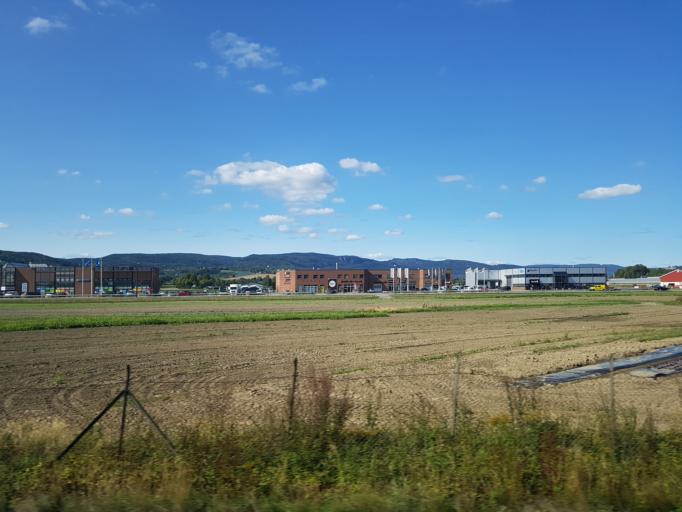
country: NO
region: Buskerud
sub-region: Lier
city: Lierbyen
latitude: 59.7568
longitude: 10.2718
